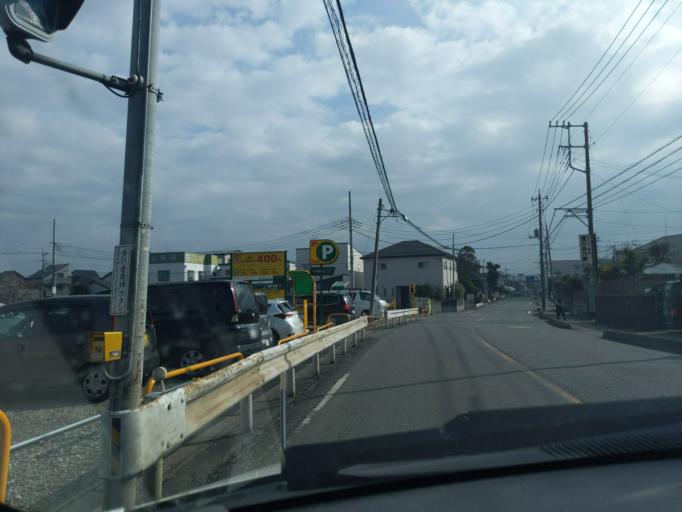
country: JP
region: Saitama
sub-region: Kawaguchi-shi
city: Hatogaya-honcho
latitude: 35.8572
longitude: 139.7528
